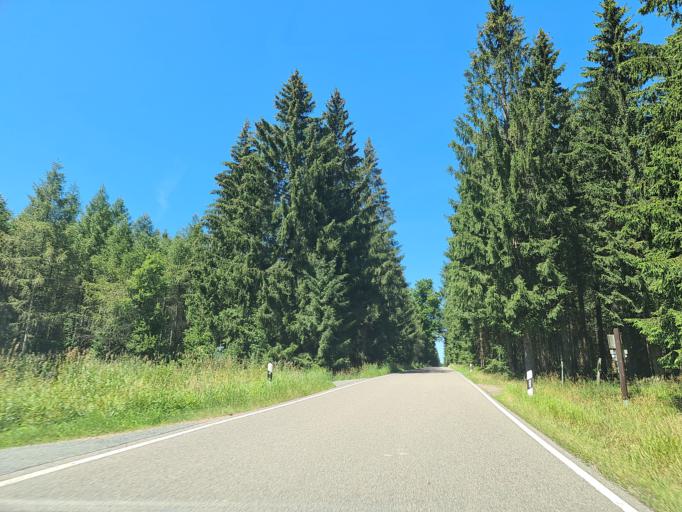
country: DE
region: Saxony
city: Rechenberg-Bienenmuhle
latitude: 50.7160
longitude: 13.5318
